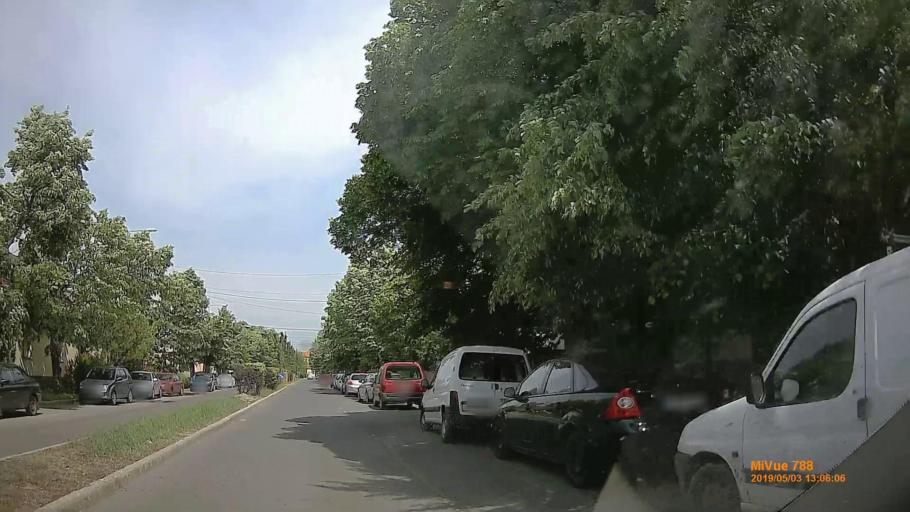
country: HU
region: Jasz-Nagykun-Szolnok
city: Szolnok
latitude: 47.1739
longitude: 20.1790
